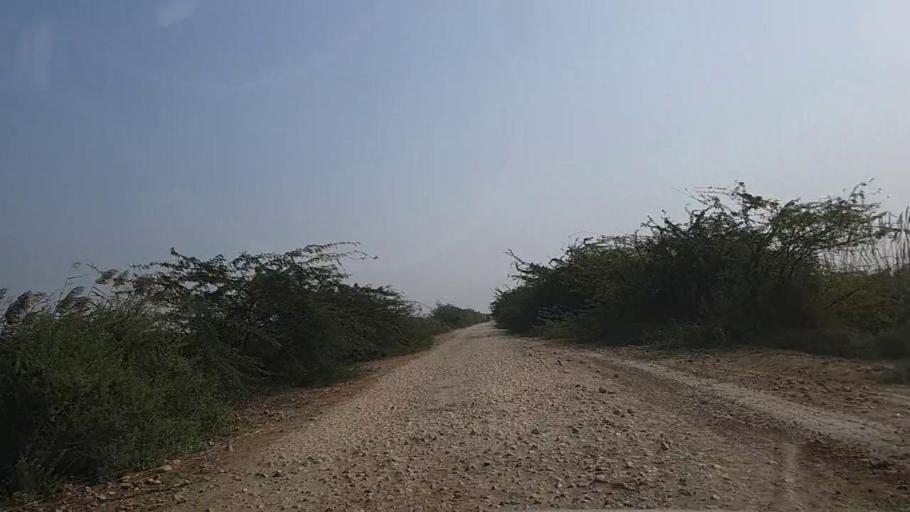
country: PK
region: Sindh
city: Keti Bandar
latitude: 24.2497
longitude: 67.6308
